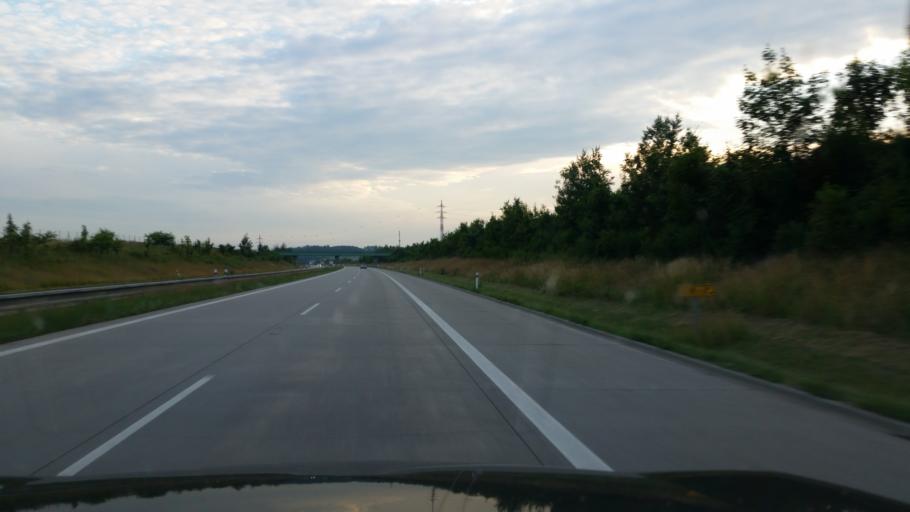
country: CZ
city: Bilovec
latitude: 49.7394
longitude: 18.0459
